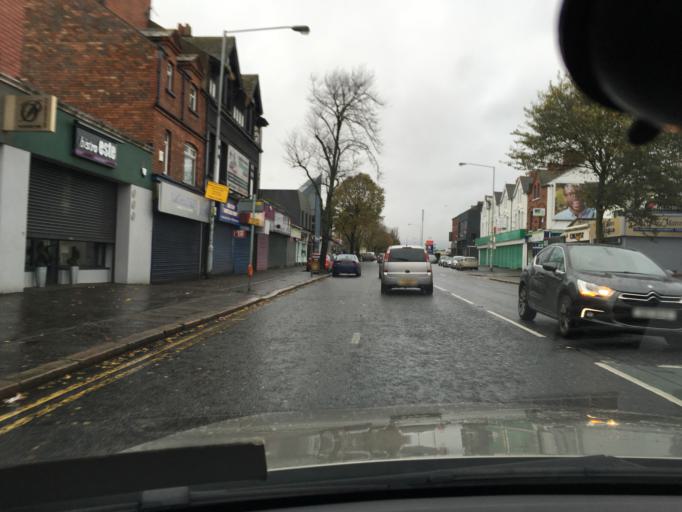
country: GB
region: Northern Ireland
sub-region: Castlereagh District
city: Castlereagh
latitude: 54.5952
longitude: -5.8690
